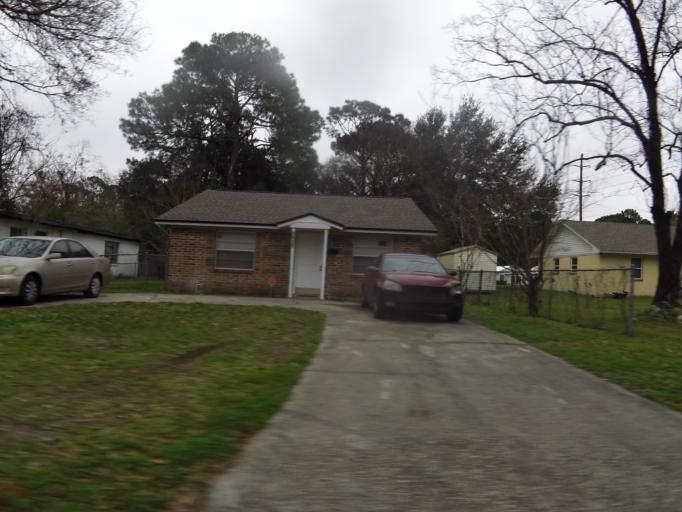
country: US
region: Florida
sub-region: Duval County
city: Jacksonville
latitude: 30.3599
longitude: -81.6998
